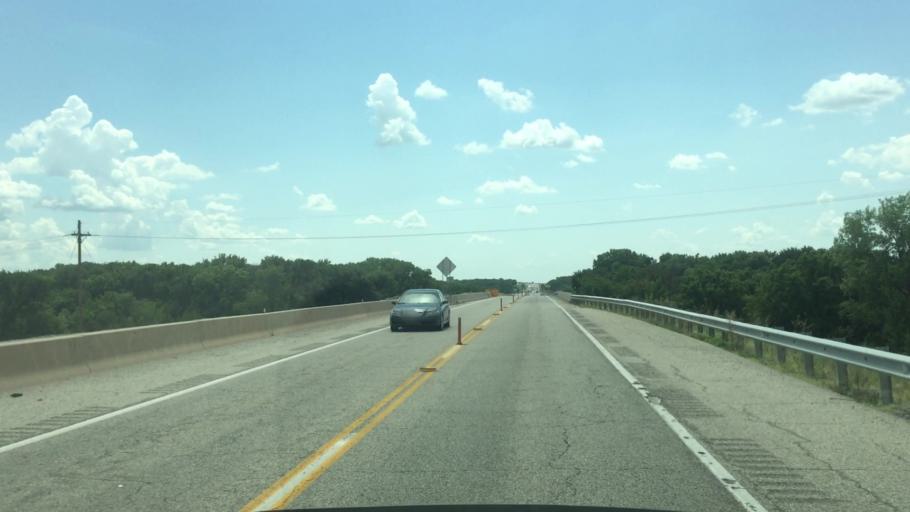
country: US
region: Kansas
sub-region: Lyon County
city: Emporia
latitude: 38.4522
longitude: -96.2016
